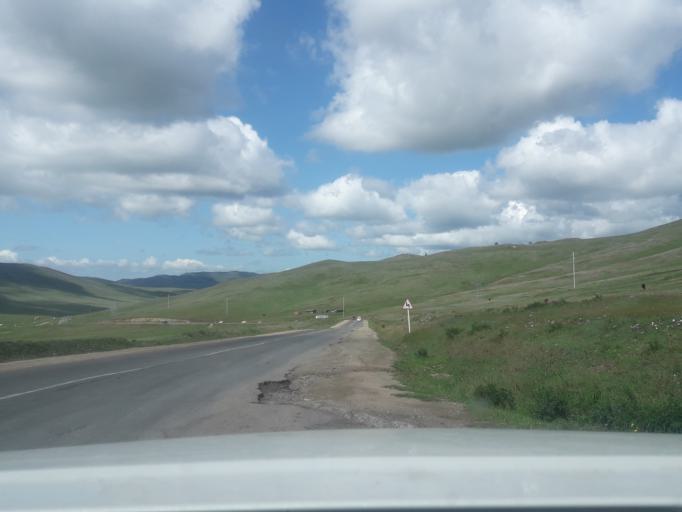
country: MN
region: Central Aimak
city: Ihsueuej
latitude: 48.1349
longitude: 106.4247
